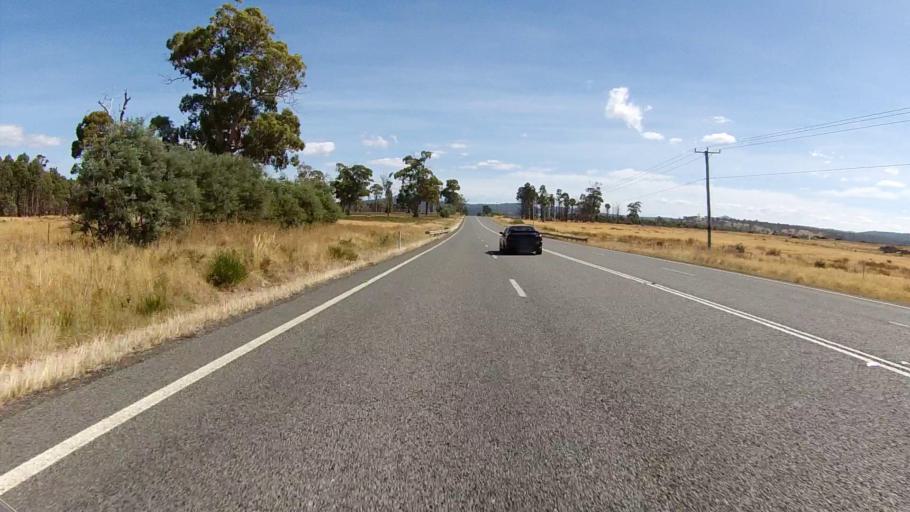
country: AU
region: Tasmania
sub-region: Sorell
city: Sorell
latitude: -42.5999
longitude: 147.7607
